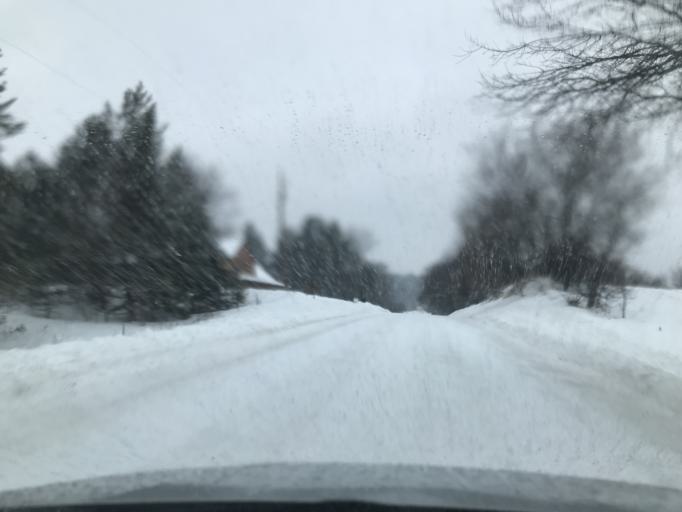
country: US
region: Wisconsin
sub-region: Marinette County
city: Peshtigo
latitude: 45.3813
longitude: -87.9415
